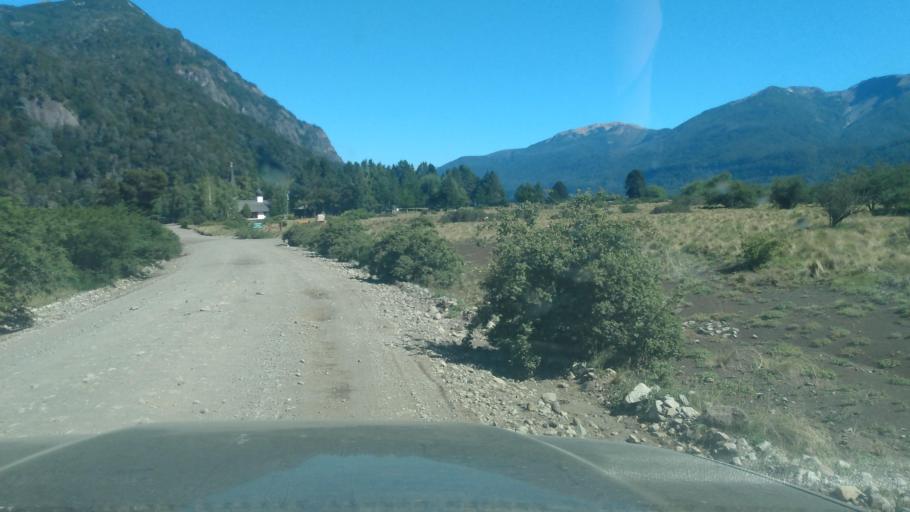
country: AR
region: Neuquen
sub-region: Departamento de Lacar
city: San Martin de los Andes
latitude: -39.7446
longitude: -71.5217
